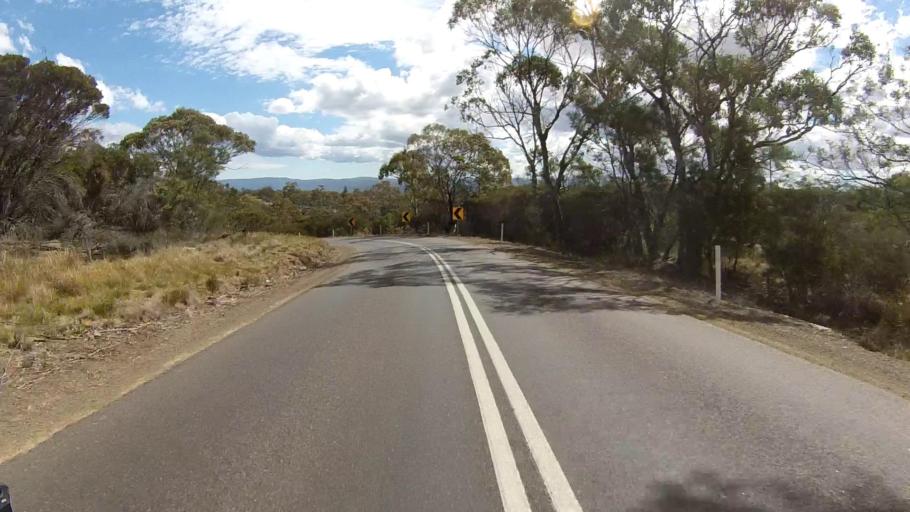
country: AU
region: Tasmania
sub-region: Break O'Day
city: St Helens
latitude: -41.9897
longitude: 148.1236
